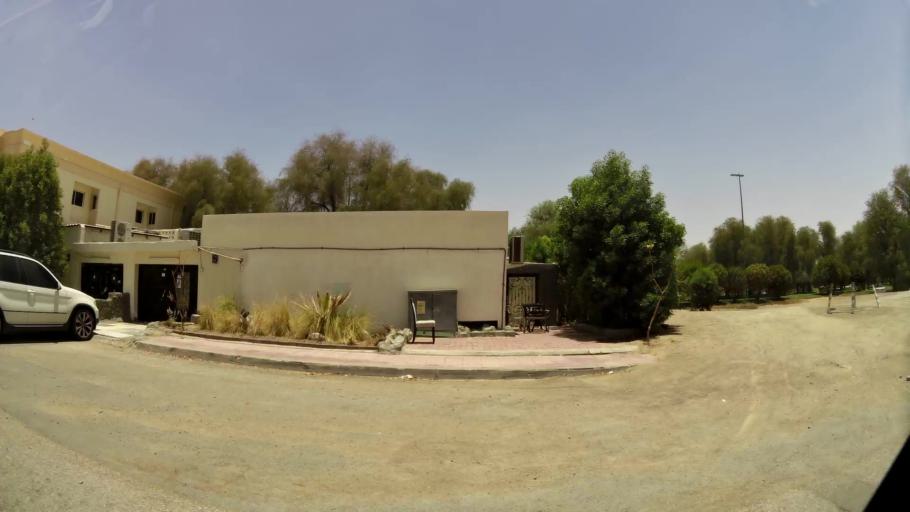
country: OM
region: Al Buraimi
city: Al Buraymi
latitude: 24.2595
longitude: 55.7327
